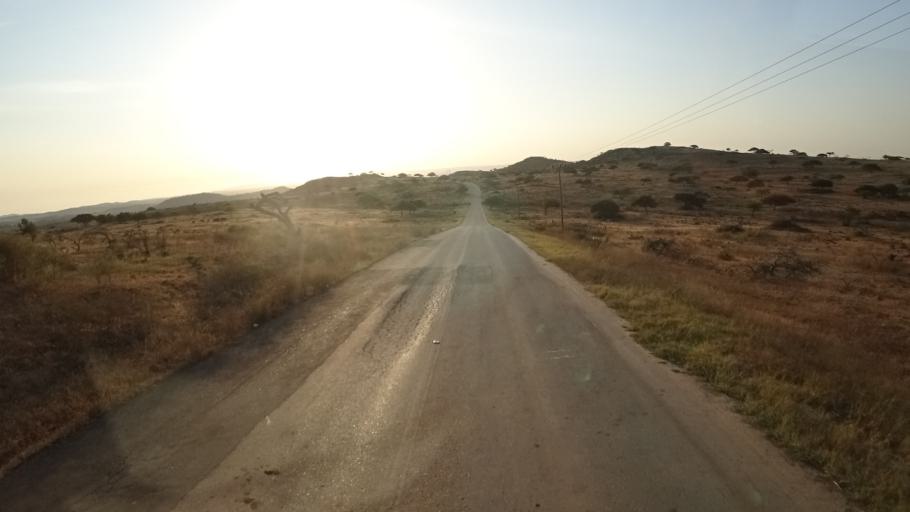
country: OM
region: Zufar
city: Salalah
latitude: 17.1478
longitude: 54.6085
